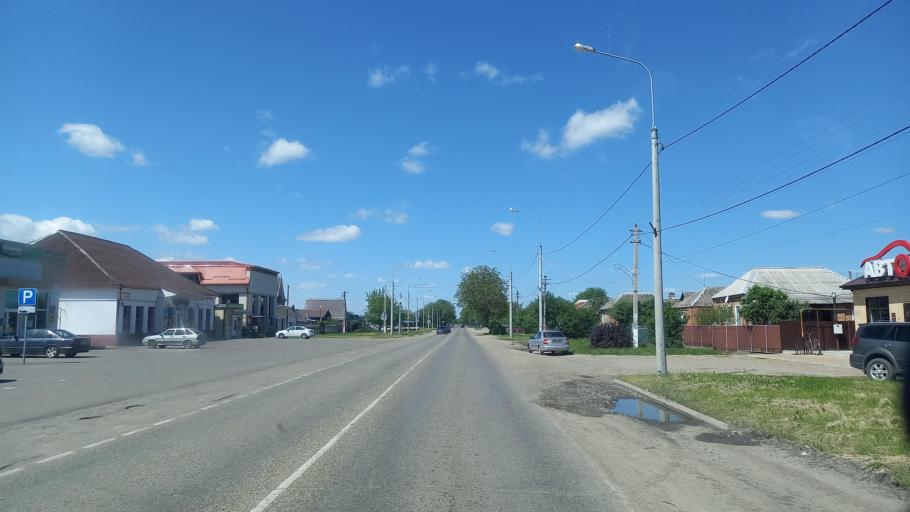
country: RU
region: Krasnodarskiy
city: Novoukrainskoye
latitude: 45.3803
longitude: 40.5235
